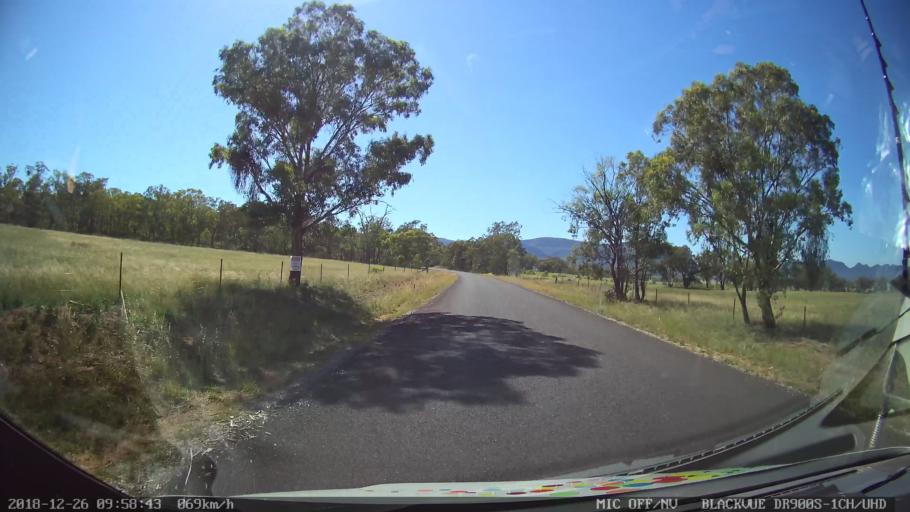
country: AU
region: New South Wales
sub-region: Mid-Western Regional
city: Kandos
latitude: -33.0401
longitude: 150.2076
